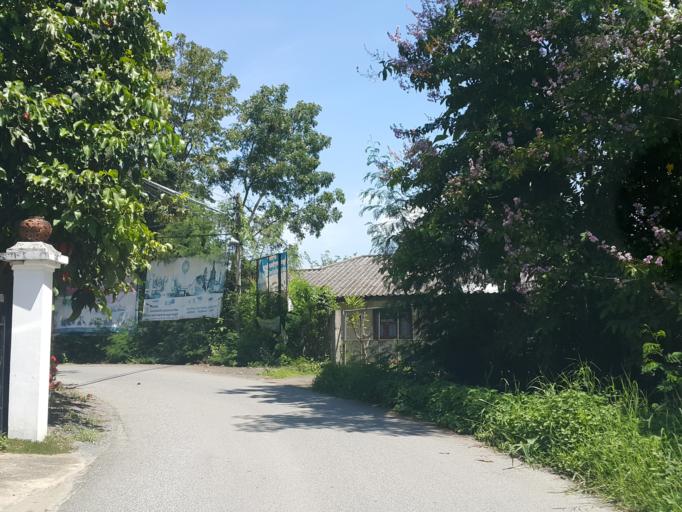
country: TH
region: Chiang Mai
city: San Sai
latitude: 18.8103
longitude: 99.0975
